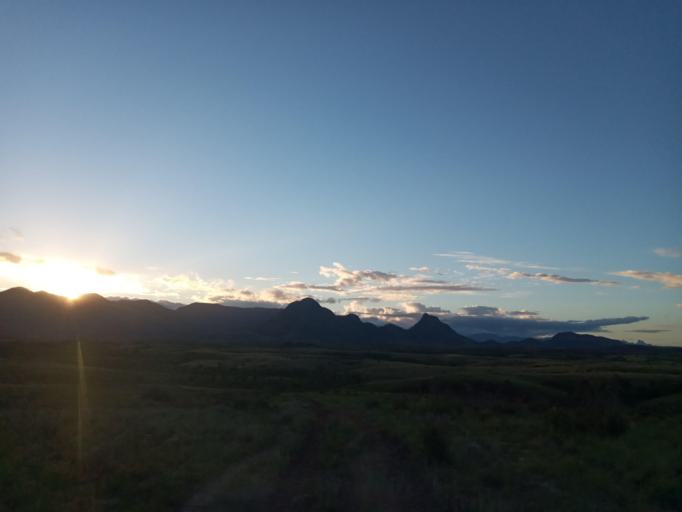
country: MG
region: Anosy
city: Fort Dauphin
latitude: -24.5131
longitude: 47.2390
